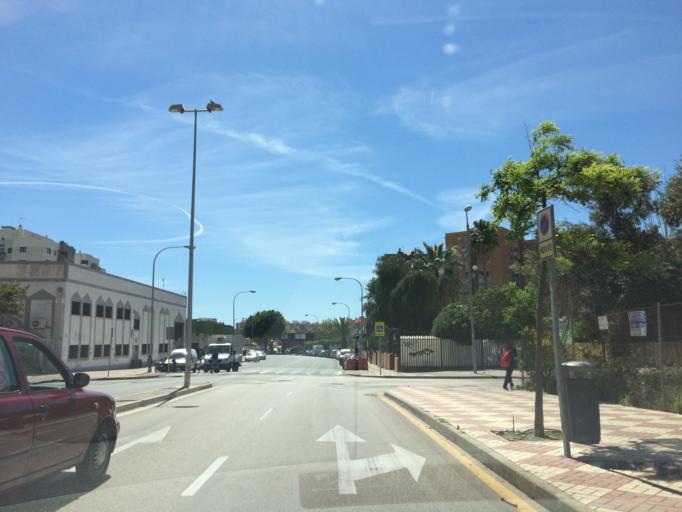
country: ES
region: Andalusia
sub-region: Provincia de Malaga
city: Malaga
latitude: 36.7068
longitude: -4.4550
